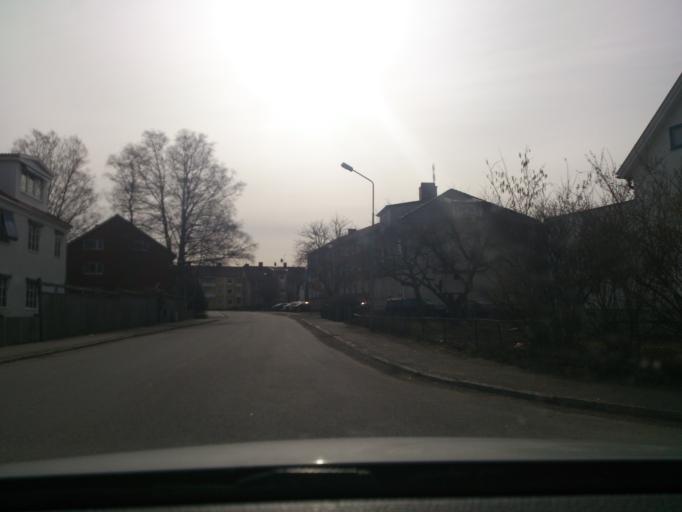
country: SE
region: Kronoberg
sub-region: Alvesta Kommun
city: Alvesta
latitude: 56.9043
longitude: 14.5569
